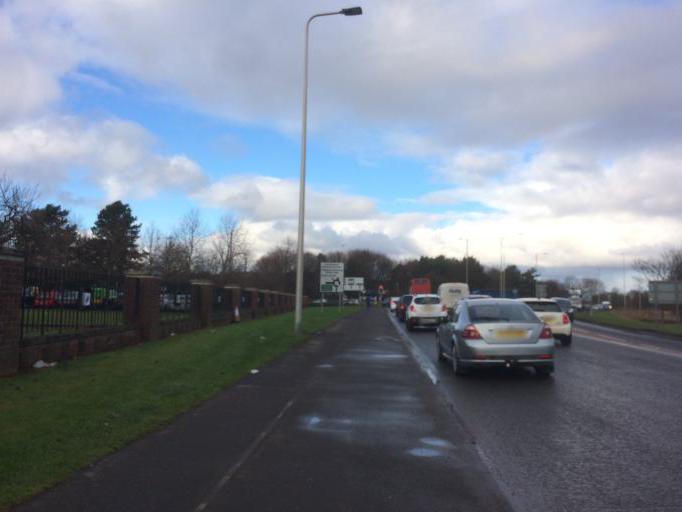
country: GB
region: Scotland
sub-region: Perth and Kinross
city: Luncarty
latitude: 56.4178
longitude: -3.4636
